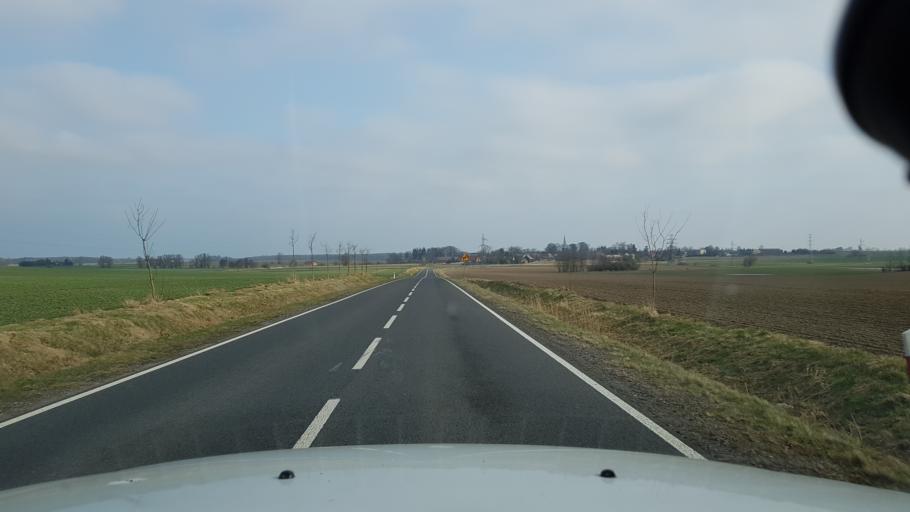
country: PL
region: West Pomeranian Voivodeship
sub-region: Powiat koszalinski
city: Sianow
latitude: 54.2850
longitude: 16.2710
